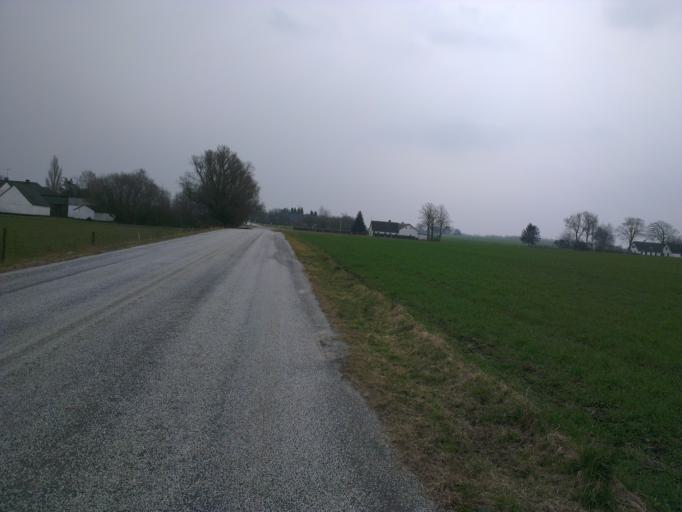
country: DK
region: Capital Region
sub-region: Egedal Kommune
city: Olstykke
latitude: 55.8072
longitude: 12.1091
